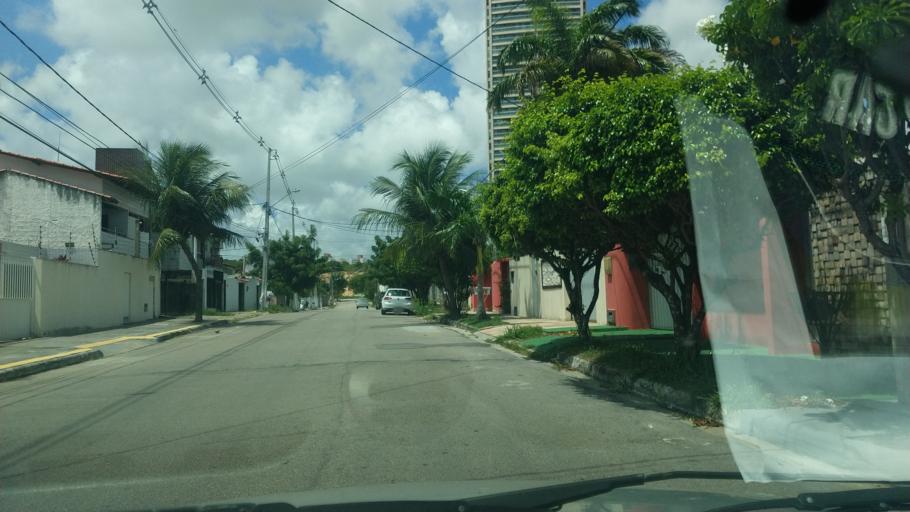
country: BR
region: Rio Grande do Norte
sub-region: Natal
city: Natal
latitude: -5.8688
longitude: -35.1926
